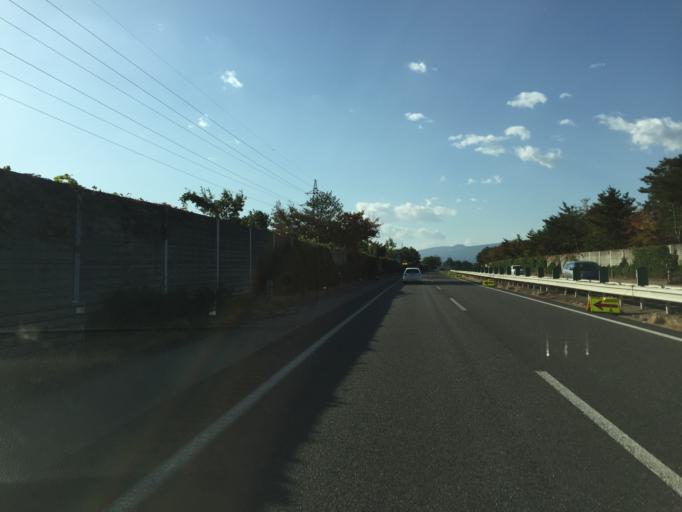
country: JP
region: Fukushima
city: Fukushima-shi
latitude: 37.7711
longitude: 140.4129
